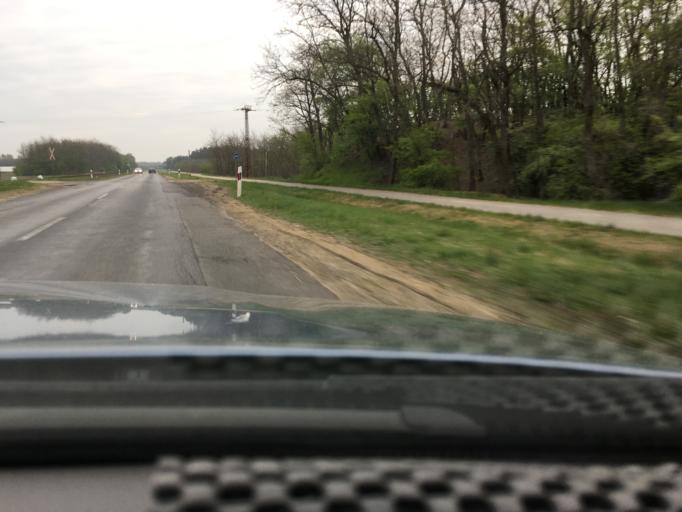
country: HU
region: Hajdu-Bihar
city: Hajdusamson
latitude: 47.6203
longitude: 21.7771
